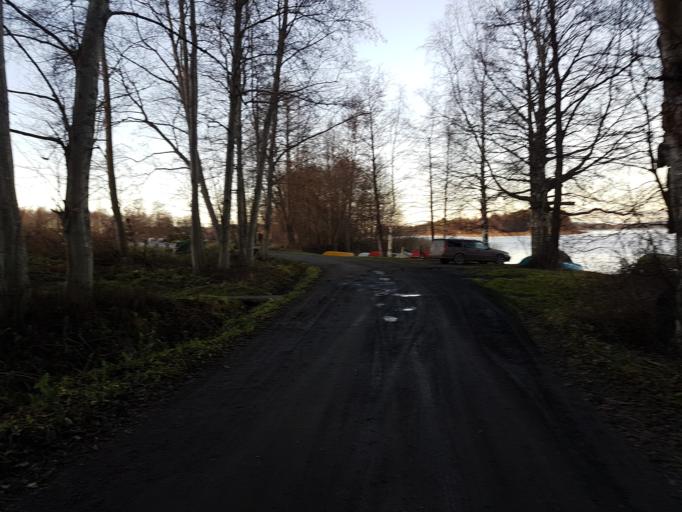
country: FI
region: Northern Savo
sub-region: Kuopio
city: Kuopio
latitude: 62.9292
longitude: 27.6265
